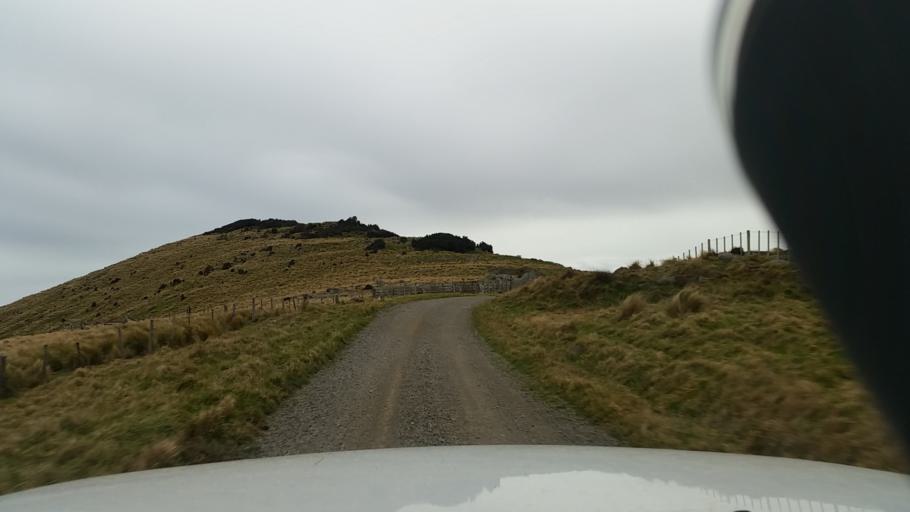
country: NZ
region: Canterbury
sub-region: Christchurch City
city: Christchurch
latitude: -43.8161
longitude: 172.7656
